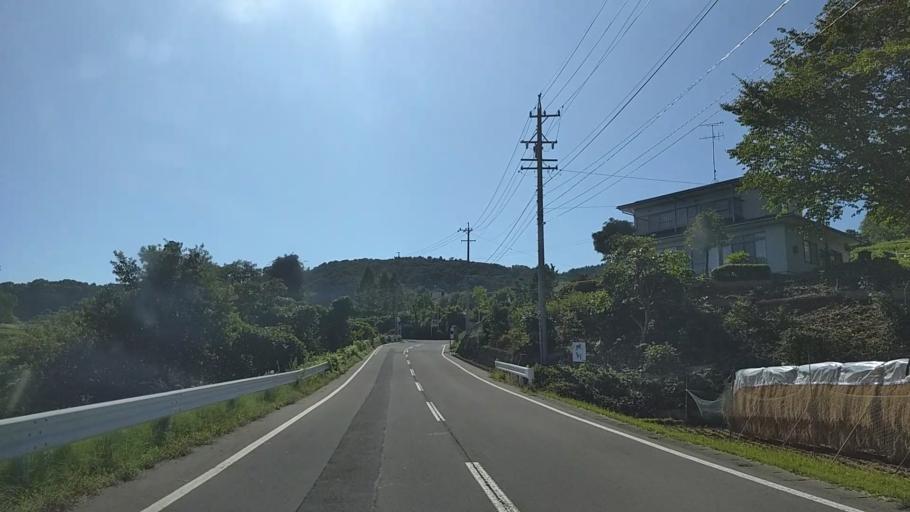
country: JP
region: Nagano
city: Nagano-shi
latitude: 36.5791
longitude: 138.1117
